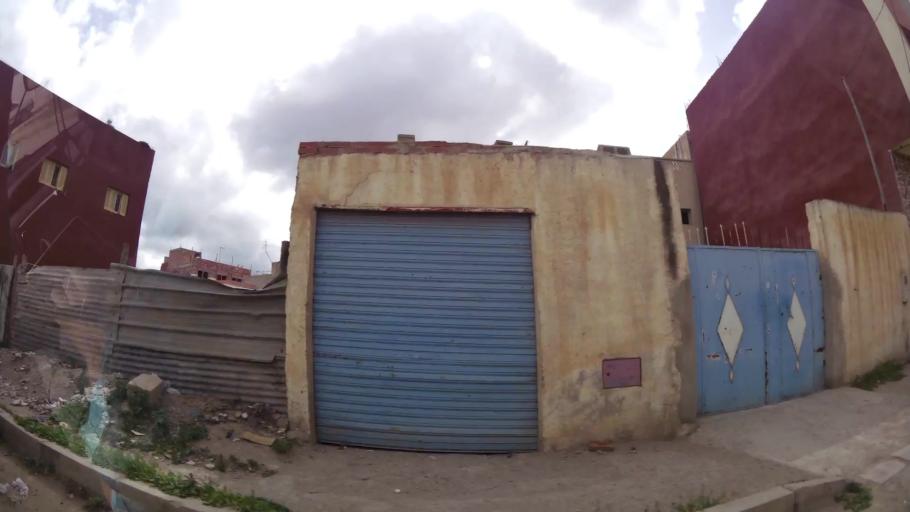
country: MA
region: Oriental
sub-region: Nador
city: Nador
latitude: 35.1598
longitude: -2.9393
